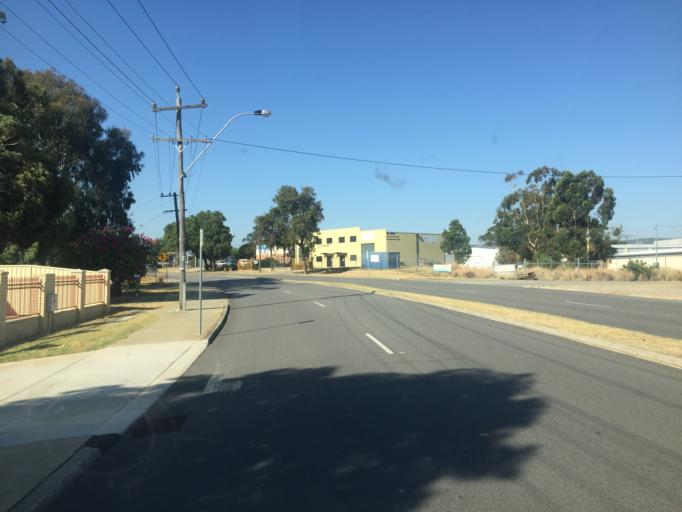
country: AU
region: Western Australia
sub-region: Gosnells
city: Maddington
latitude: -32.0415
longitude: 115.9815
